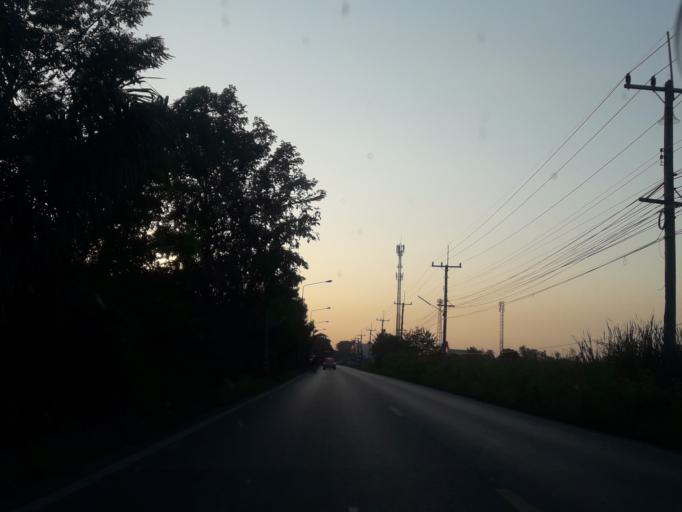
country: TH
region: Pathum Thani
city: Nong Suea
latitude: 14.1313
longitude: 100.7834
